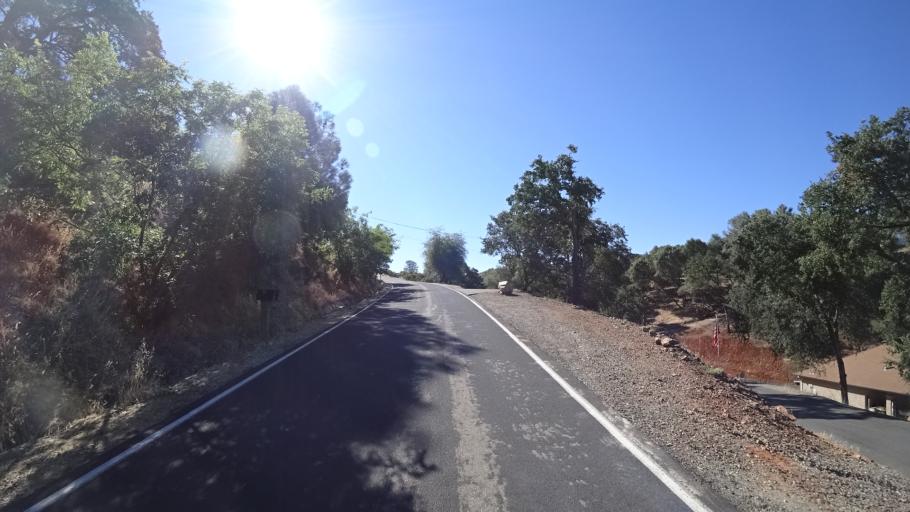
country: US
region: California
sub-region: Calaveras County
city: Rancho Calaveras
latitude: 38.1123
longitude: -120.8624
